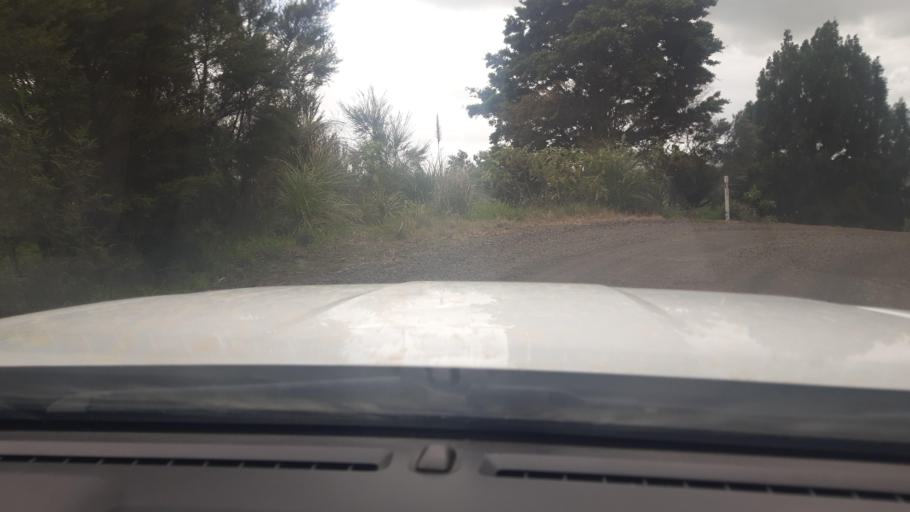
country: NZ
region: Northland
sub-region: Far North District
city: Kaitaia
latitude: -35.0762
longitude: 173.3220
